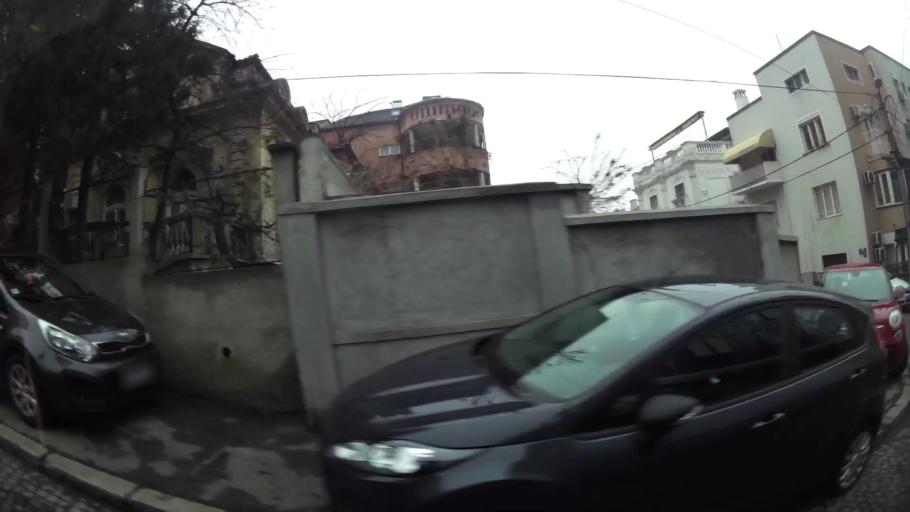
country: RS
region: Central Serbia
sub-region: Belgrade
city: Savski Venac
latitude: 44.7963
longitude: 20.4462
